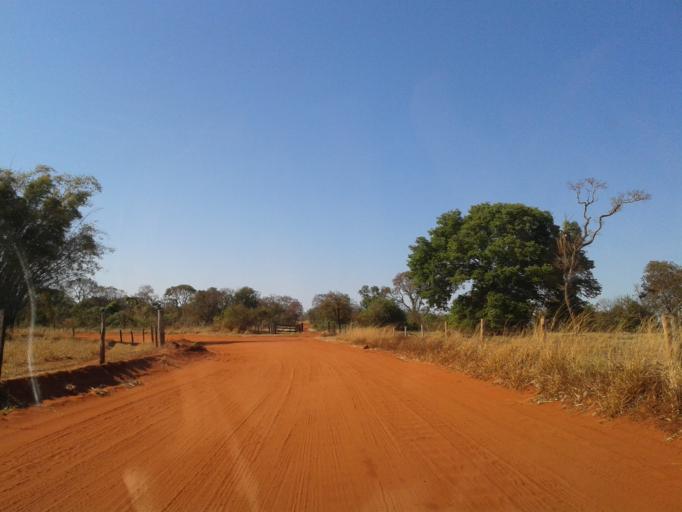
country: BR
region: Minas Gerais
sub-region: Ituiutaba
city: Ituiutaba
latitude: -19.0472
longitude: -49.2871
